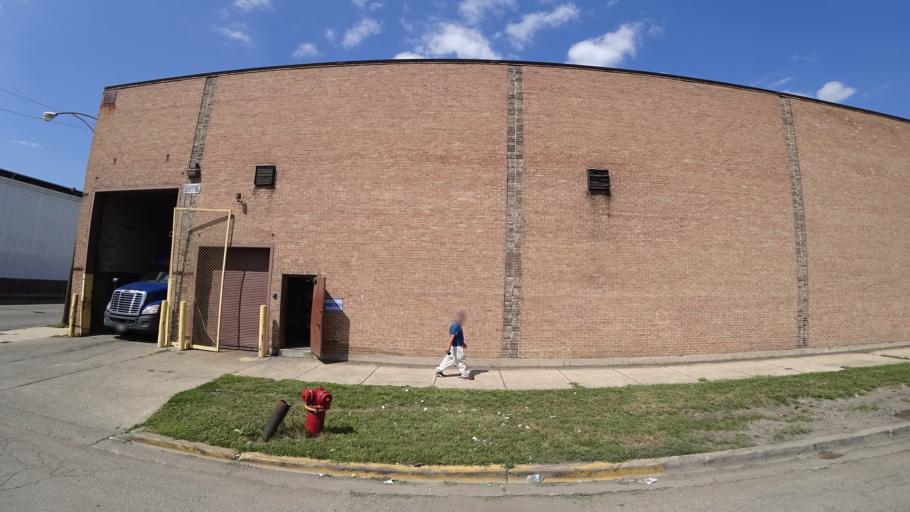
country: US
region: Illinois
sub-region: Cook County
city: Cicero
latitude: 41.8579
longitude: -87.7344
